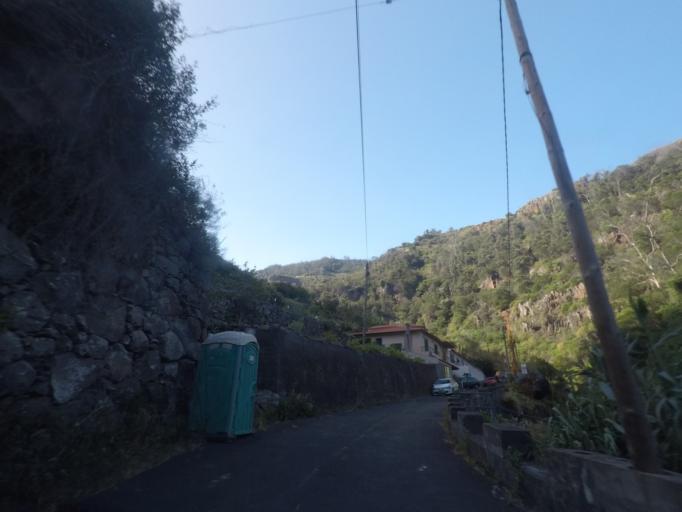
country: PT
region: Madeira
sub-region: Santa Cruz
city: Santa Cruz
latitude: 32.6941
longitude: -16.8057
